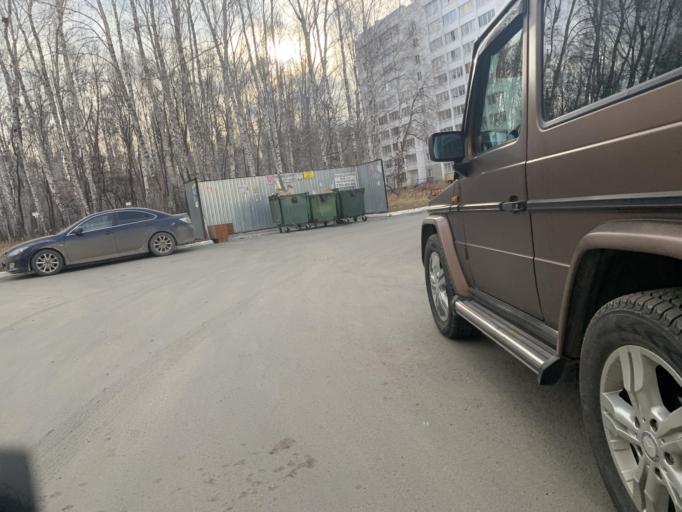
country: RU
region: Chelyabinsk
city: Roshchino
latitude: 55.2069
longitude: 61.3066
